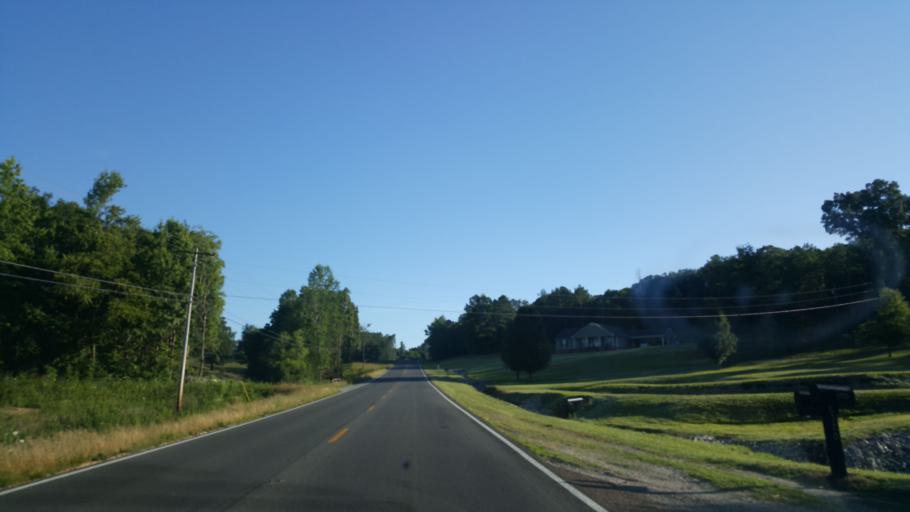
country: US
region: Tennessee
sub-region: Henderson County
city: Lexington
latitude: 35.5843
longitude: -88.3896
